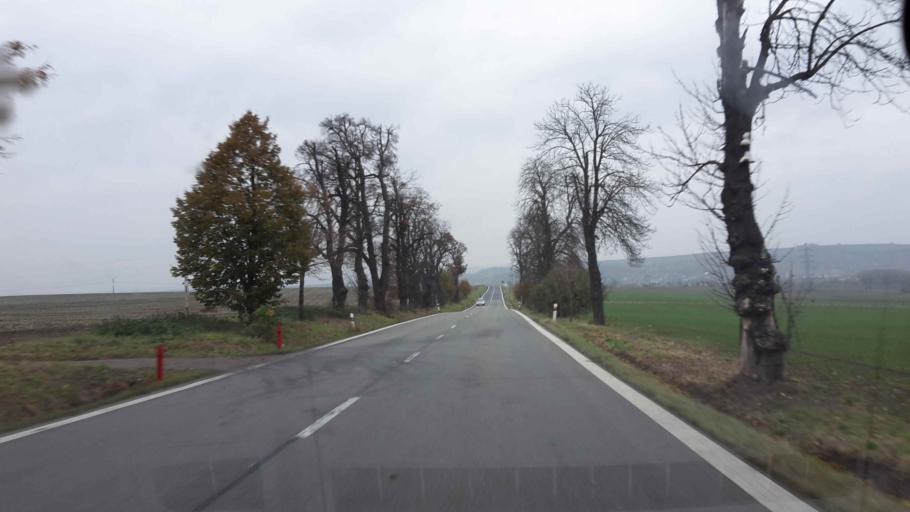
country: CZ
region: South Moravian
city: Slavkov u Brna
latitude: 49.1294
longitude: 16.8850
